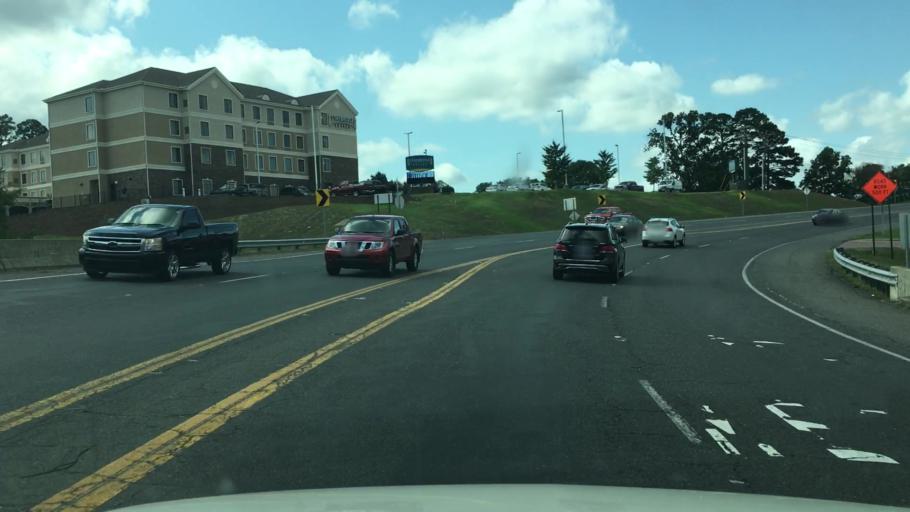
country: US
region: Arkansas
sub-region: Garland County
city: Lake Hamilton
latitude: 34.4292
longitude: -93.0848
